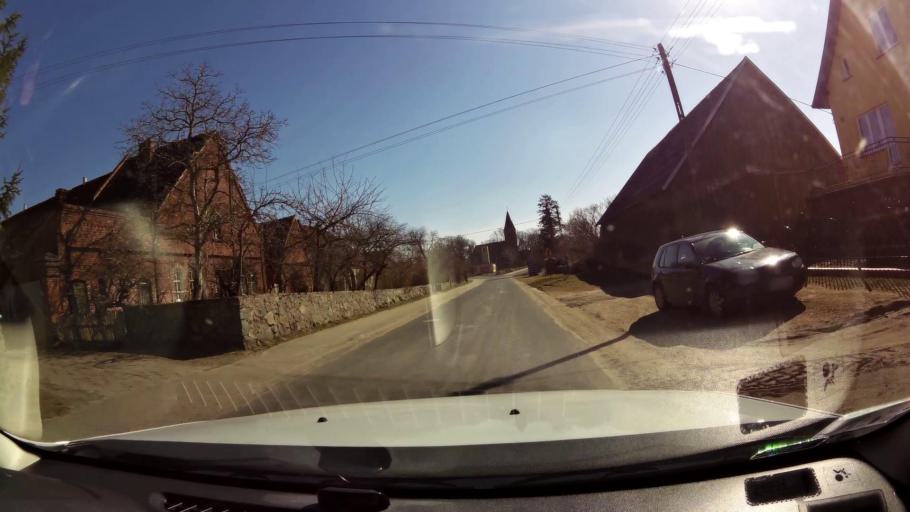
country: PL
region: West Pomeranian Voivodeship
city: Trzcinsko Zdroj
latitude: 52.9867
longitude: 14.6056
